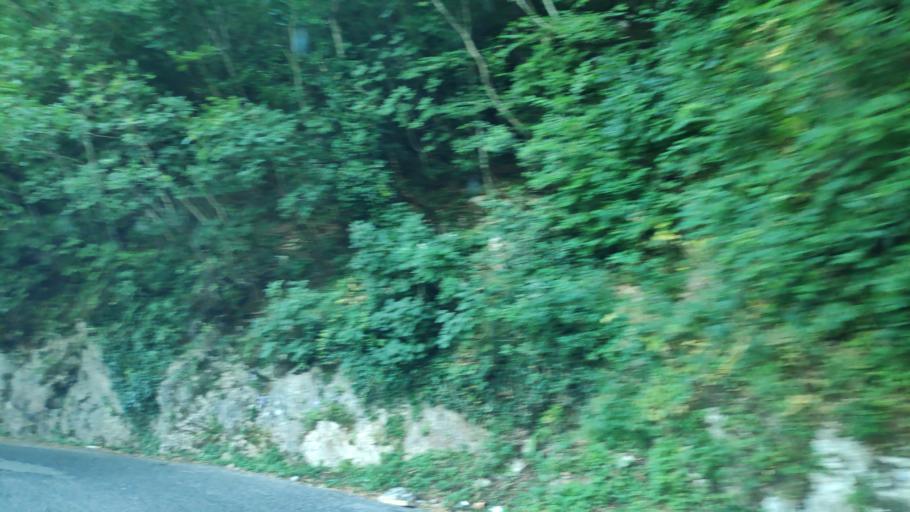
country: IT
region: Campania
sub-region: Provincia di Salerno
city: Pietre
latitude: 40.7178
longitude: 14.6120
